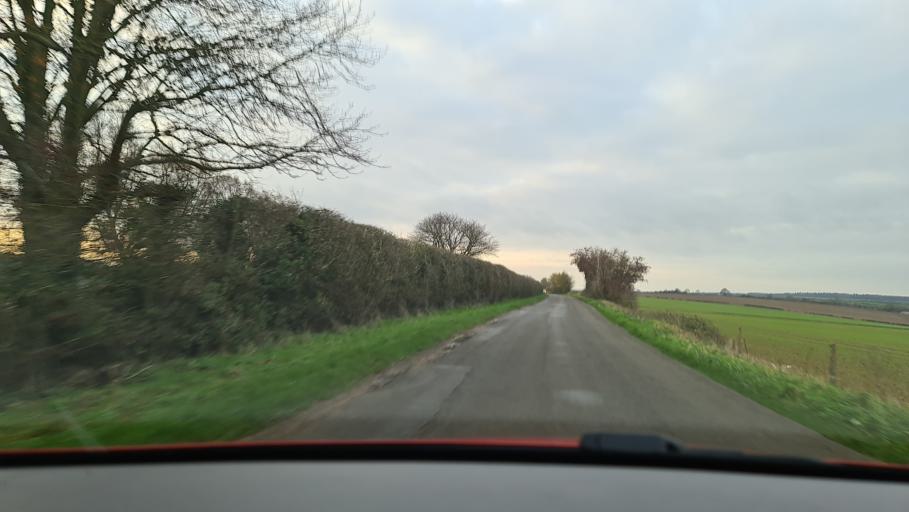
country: GB
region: England
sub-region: Oxfordshire
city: Somerton
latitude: 51.9284
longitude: -1.2712
